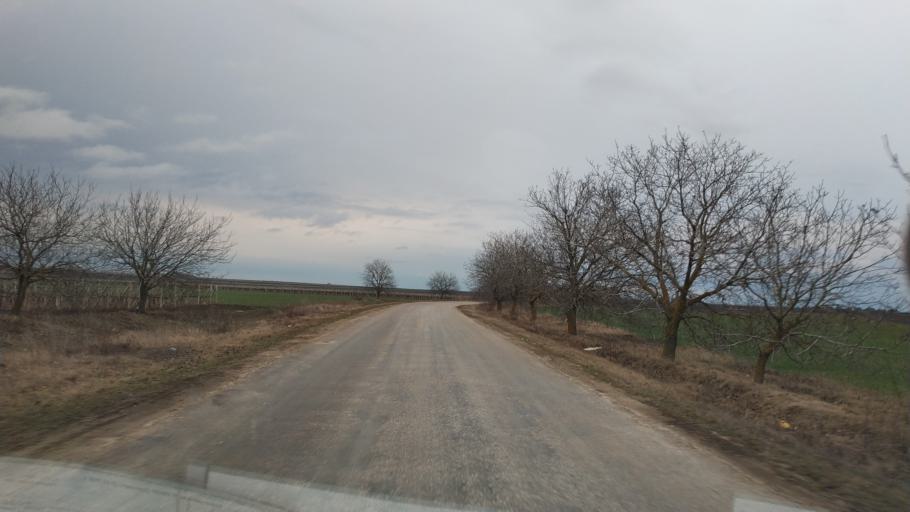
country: MD
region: Causeni
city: Causeni
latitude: 46.6098
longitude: 29.4014
